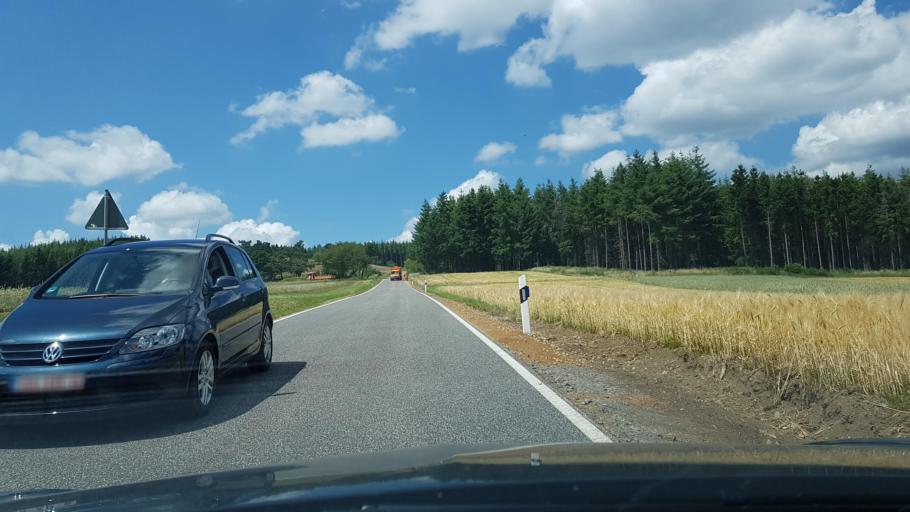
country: DE
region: Rheinland-Pfalz
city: Arft
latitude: 50.3826
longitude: 7.0747
